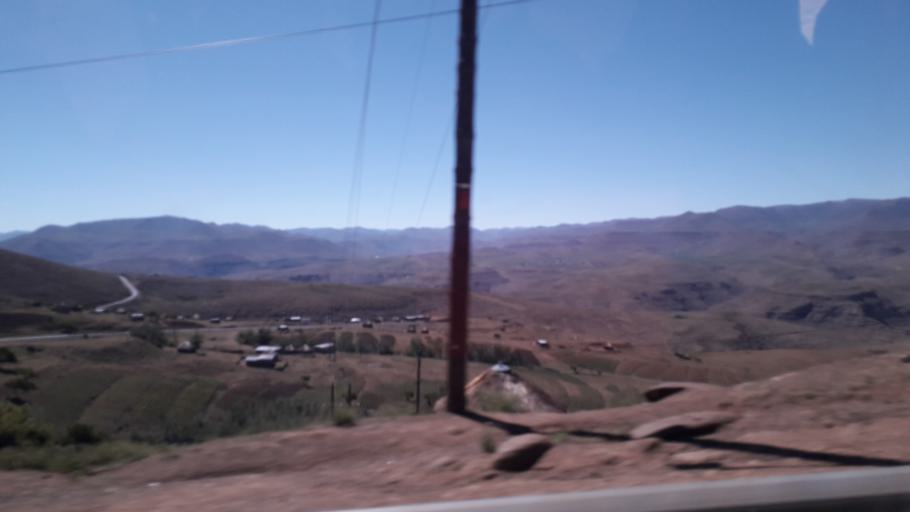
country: LS
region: Mokhotlong
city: Mokhotlong
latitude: -29.2840
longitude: 28.9477
